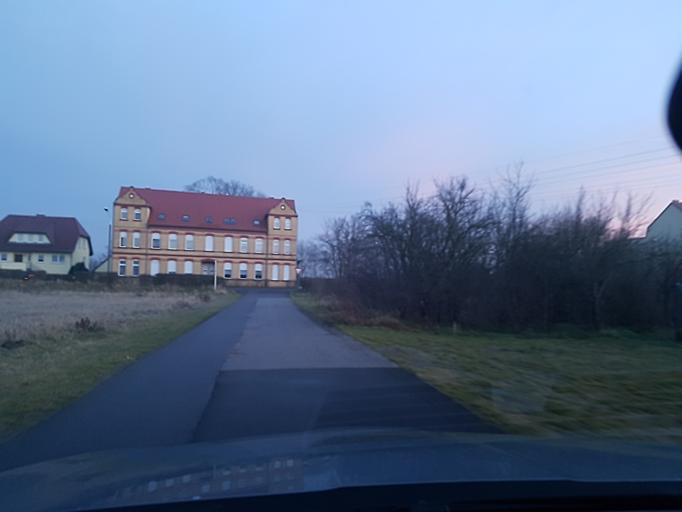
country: DE
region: Brandenburg
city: Doberlug-Kirchhain
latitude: 51.6168
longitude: 13.5578
